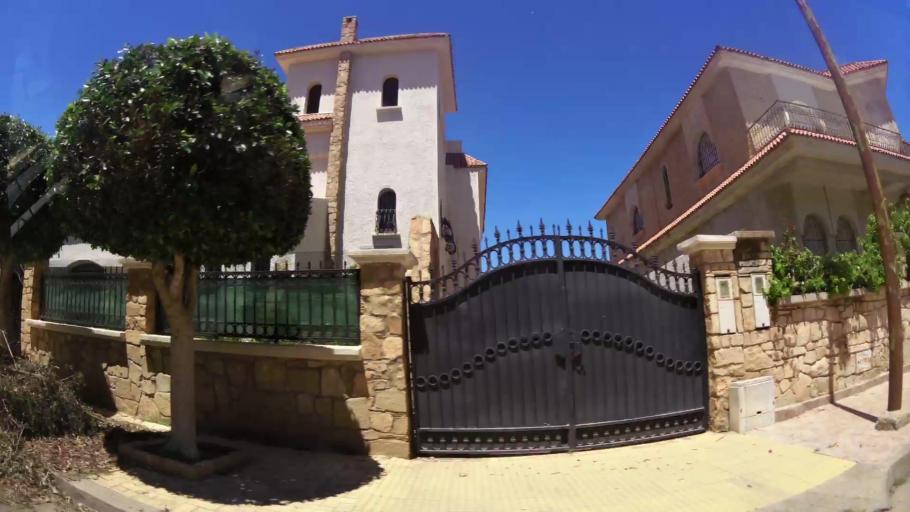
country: MA
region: Oriental
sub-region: Oujda-Angad
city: Oujda
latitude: 34.6695
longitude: -1.8730
